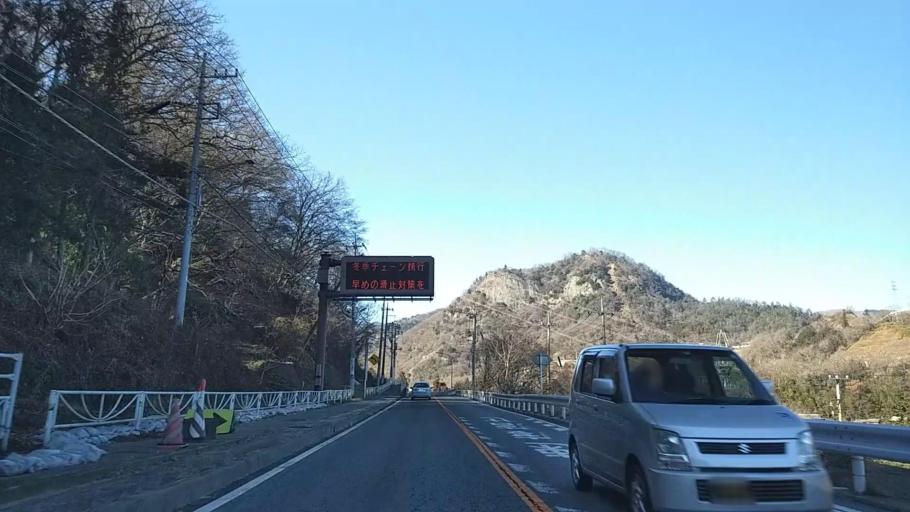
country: JP
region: Yamanashi
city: Otsuki
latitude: 35.6120
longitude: 138.9598
